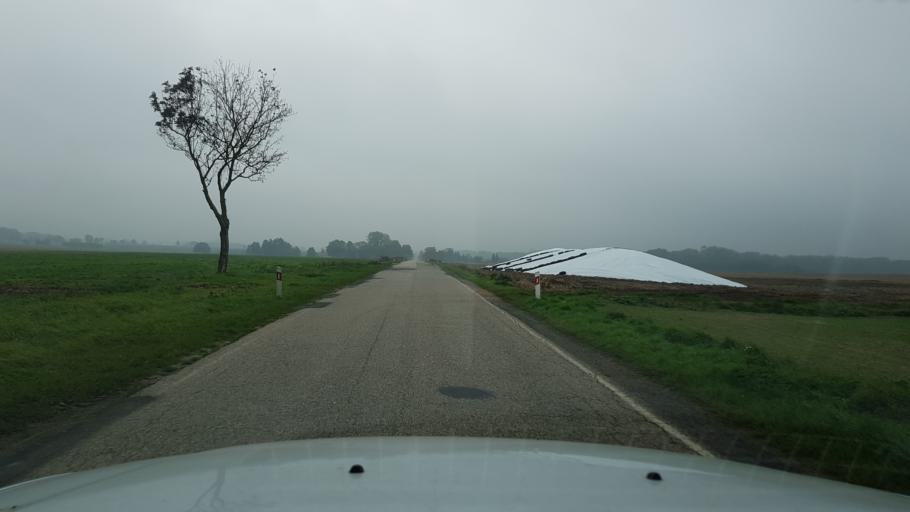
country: PL
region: West Pomeranian Voivodeship
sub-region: Powiat stargardzki
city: Dolice
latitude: 53.1680
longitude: 15.2238
